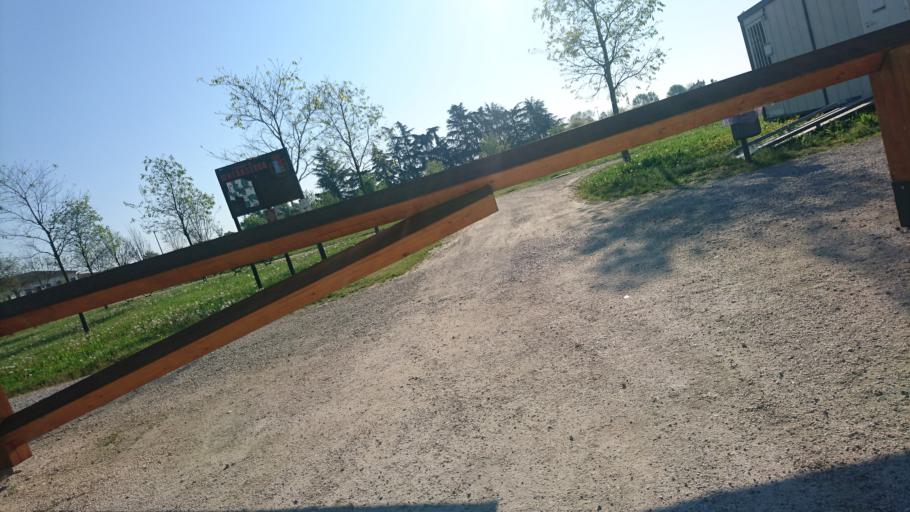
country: IT
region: Veneto
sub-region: Provincia di Padova
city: Massanzago-Ca' Baglioni-San Dono
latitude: 45.5541
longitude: 12.0030
